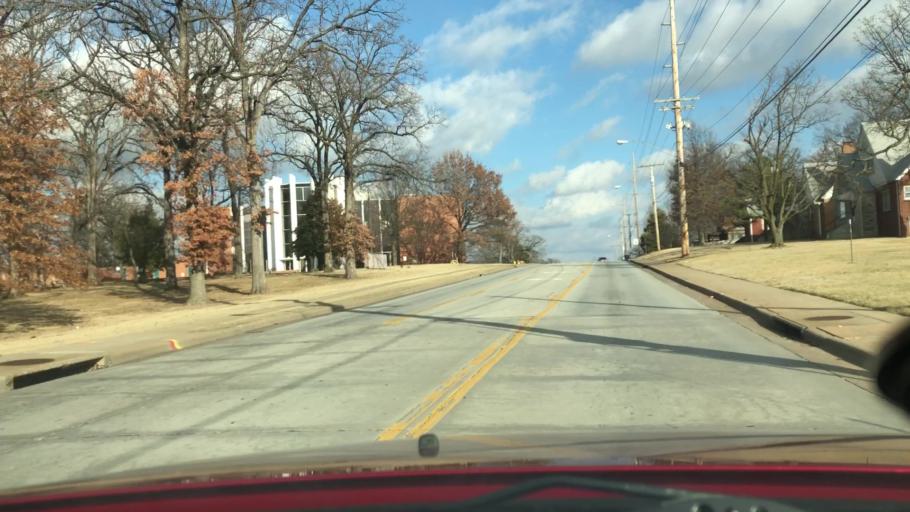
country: US
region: Missouri
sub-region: Greene County
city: Springfield
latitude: 37.2516
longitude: -93.2965
